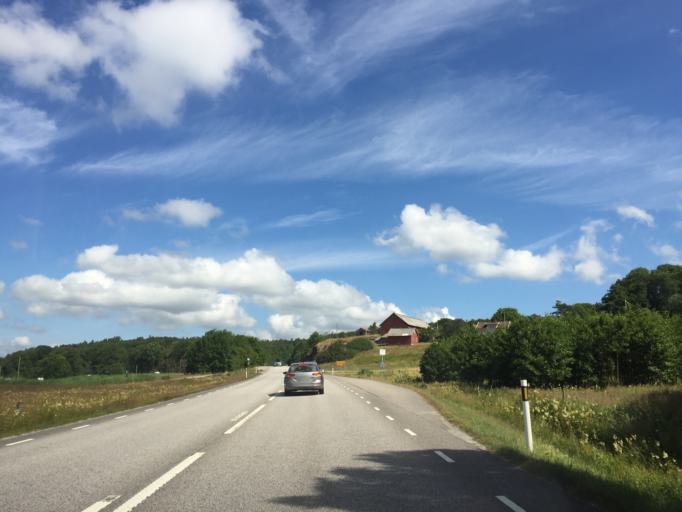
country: SE
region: Vaestra Goetaland
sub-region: Orust
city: Henan
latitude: 58.2733
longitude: 11.6938
